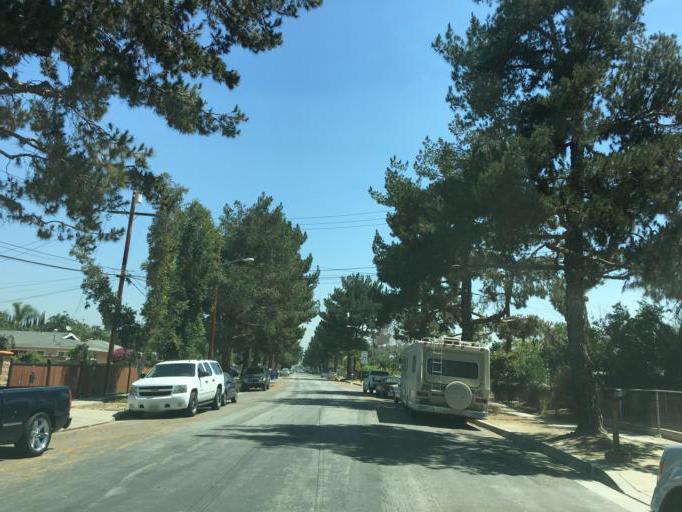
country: US
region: California
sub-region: Los Angeles County
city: Avocado Heights
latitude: 34.0469
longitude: -118.0010
